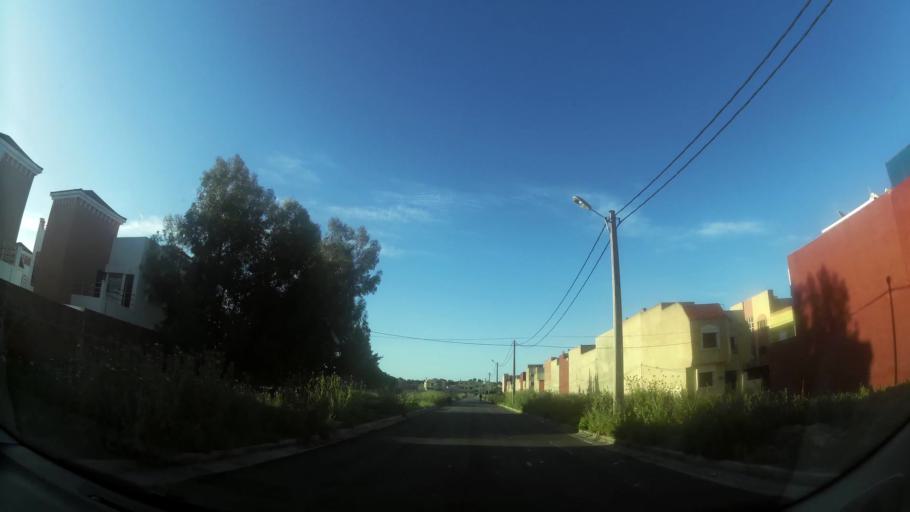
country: MA
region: Oriental
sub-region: Berkane-Taourirt
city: Madagh
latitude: 35.0821
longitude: -2.2404
